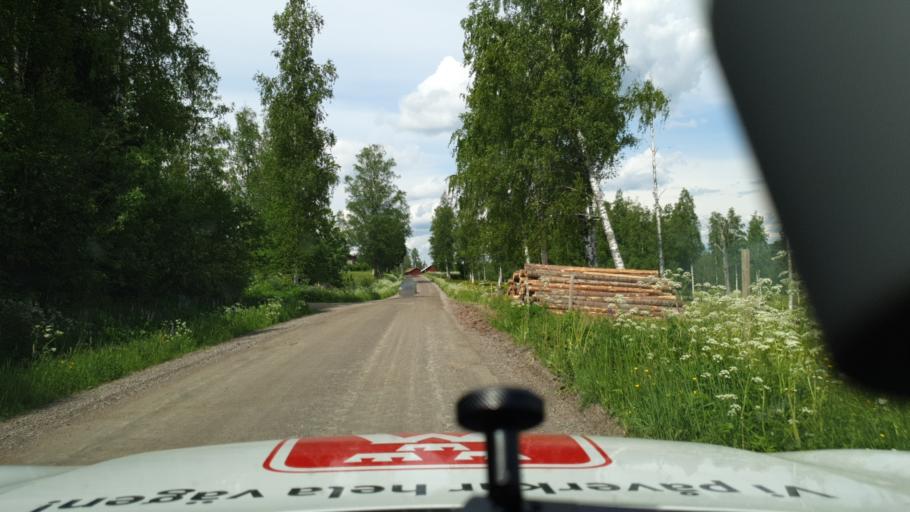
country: SE
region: Vaermland
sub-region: Torsby Kommun
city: Torsby
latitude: 59.9525
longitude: 12.8941
